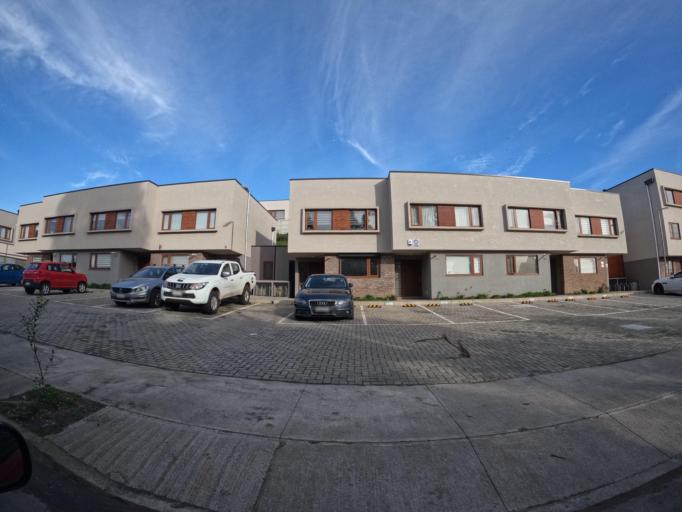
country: CL
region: Biobio
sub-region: Provincia de Concepcion
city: Concepcion
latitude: -36.7888
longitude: -73.0490
